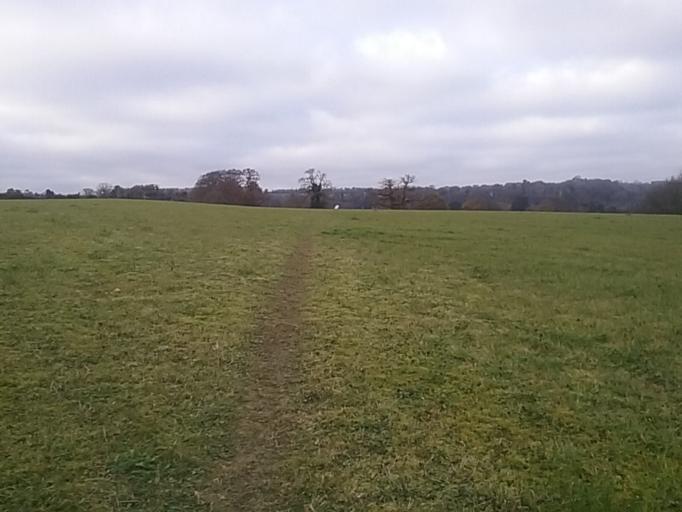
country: IE
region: Leinster
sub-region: Lu
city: Tullyallen
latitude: 53.7181
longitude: -6.4127
